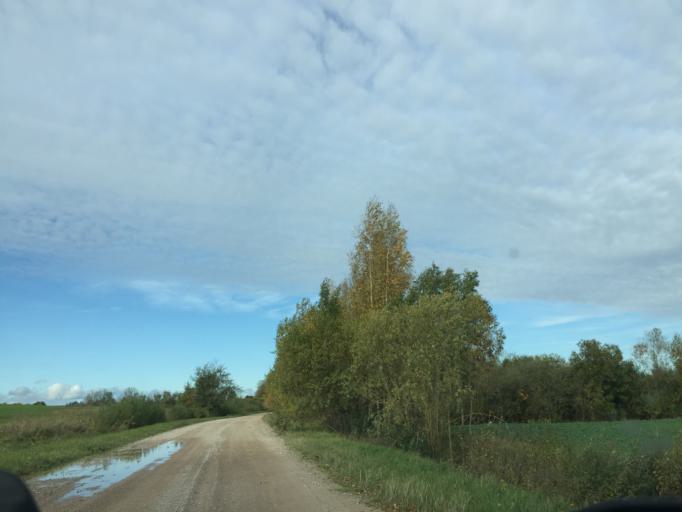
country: LV
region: Jaunpils
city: Jaunpils
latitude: 56.6197
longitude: 23.0662
